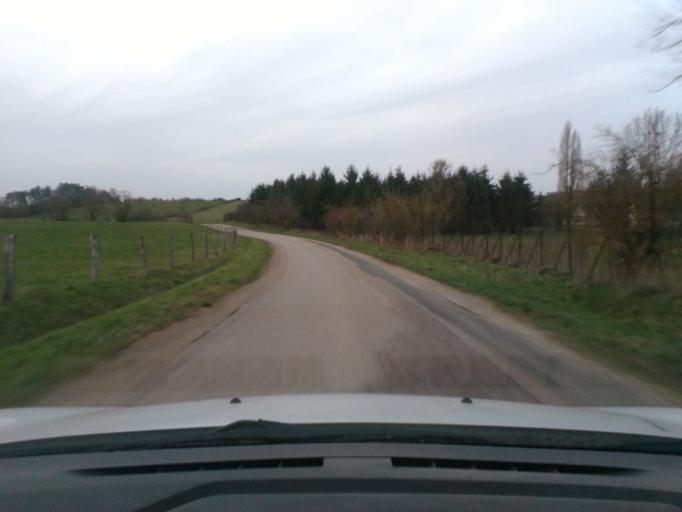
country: FR
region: Lorraine
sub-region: Departement des Vosges
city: Mirecourt
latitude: 48.2952
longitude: 6.1036
